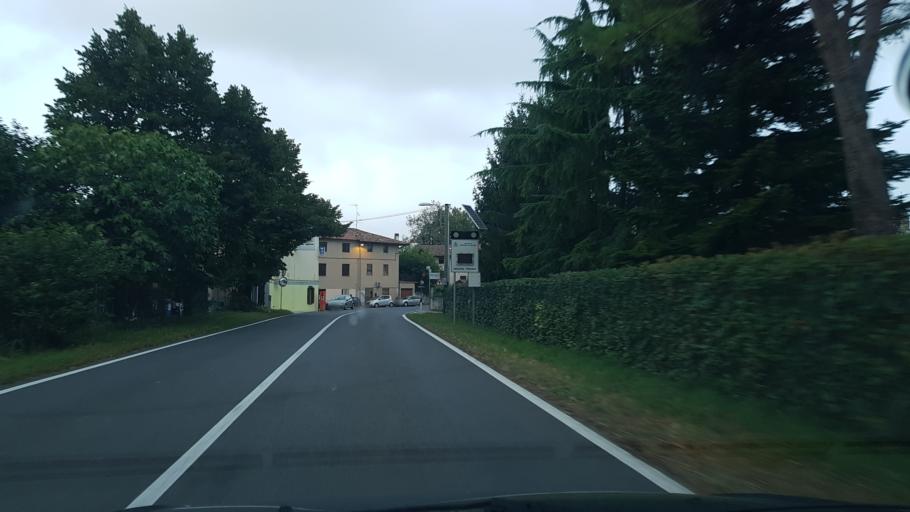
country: IT
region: Friuli Venezia Giulia
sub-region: Provincia di Gorizia
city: Medea
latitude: 45.8994
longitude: 13.4152
